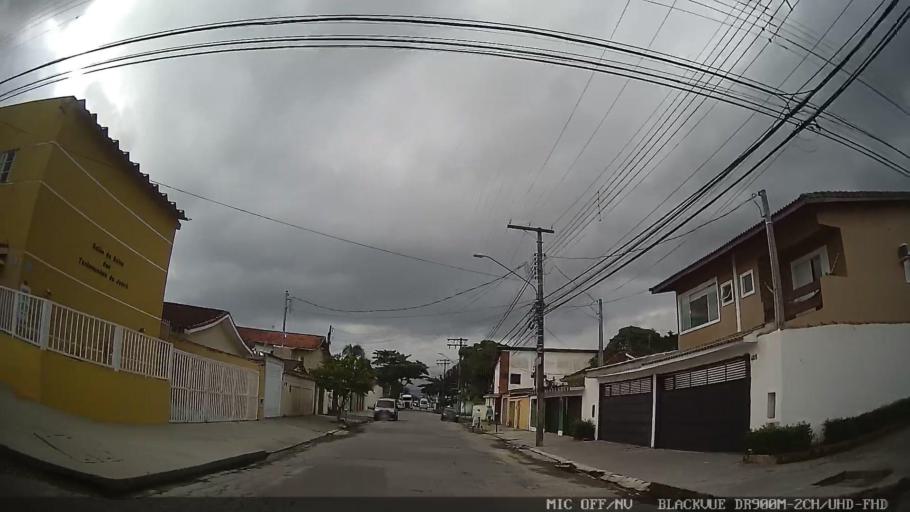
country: BR
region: Sao Paulo
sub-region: Guaruja
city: Guaruja
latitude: -23.9962
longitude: -46.2767
